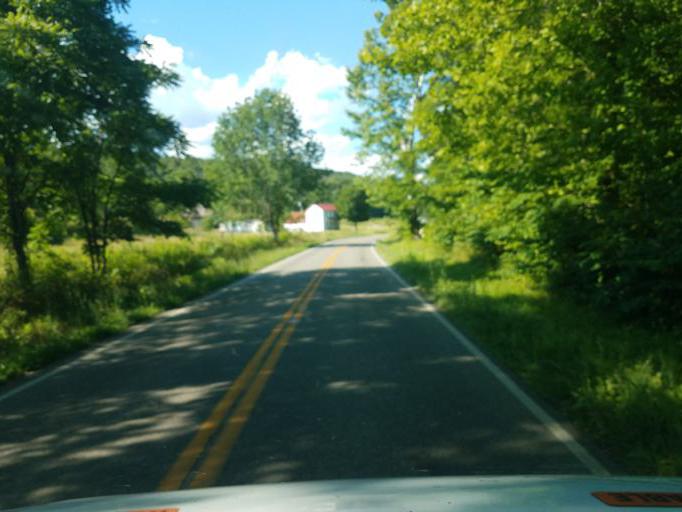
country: US
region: Ohio
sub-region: Gallia County
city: Gallipolis
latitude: 38.7768
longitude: -82.3528
